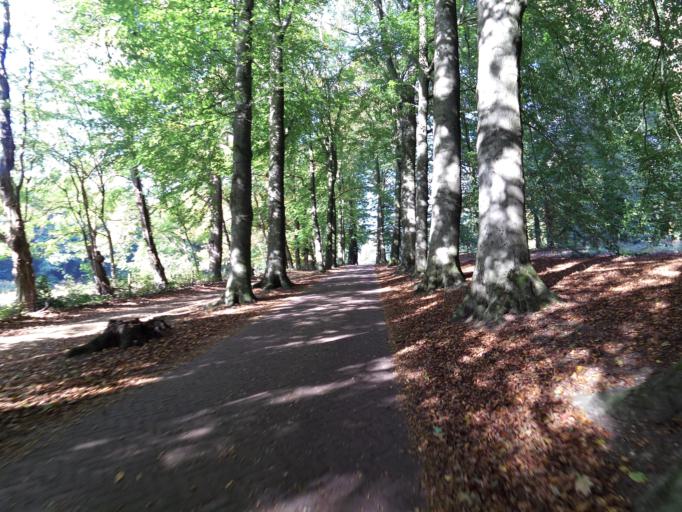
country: NL
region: Gelderland
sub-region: Gemeente Rheden
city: Rheden
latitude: 52.0179
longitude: 6.0211
